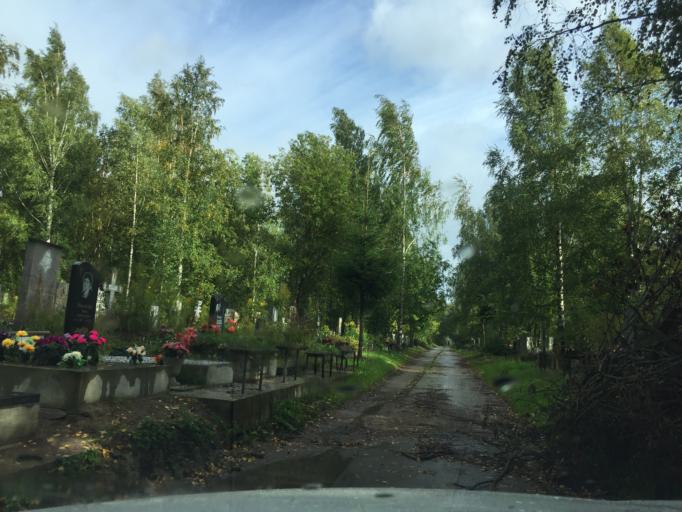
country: RU
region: St.-Petersburg
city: Aleksandrovskaya
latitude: 59.7603
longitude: 30.2746
